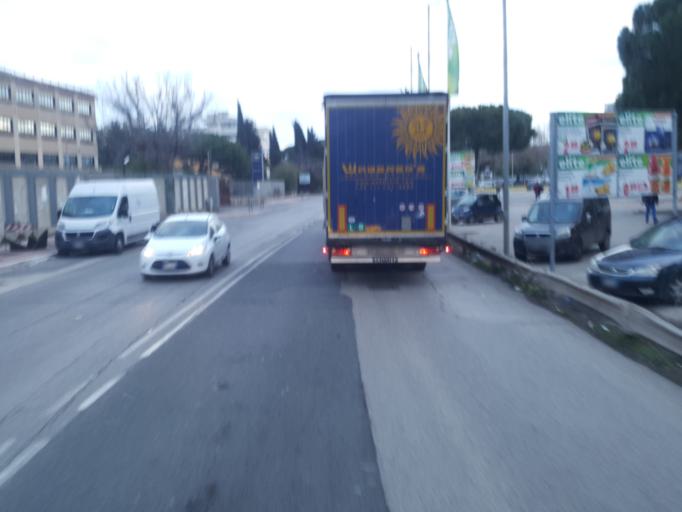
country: IT
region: Latium
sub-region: Citta metropolitana di Roma Capitale
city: Area Produttiva
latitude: 41.6777
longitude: 12.5000
